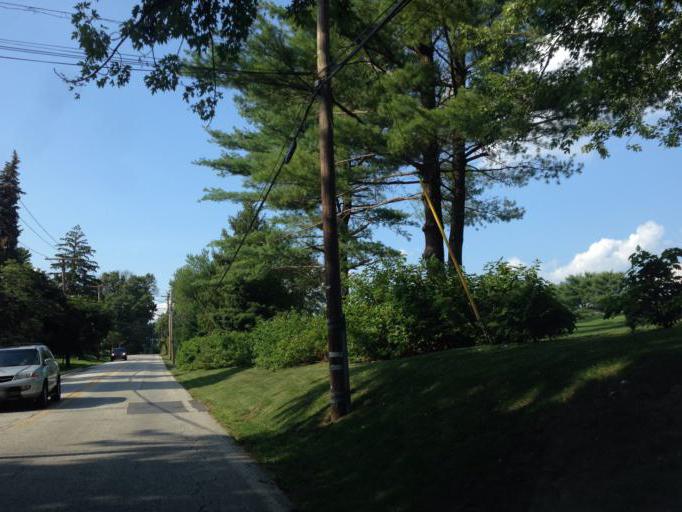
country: US
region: Maryland
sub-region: Baltimore County
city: Towson
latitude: 39.3871
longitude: -76.5904
